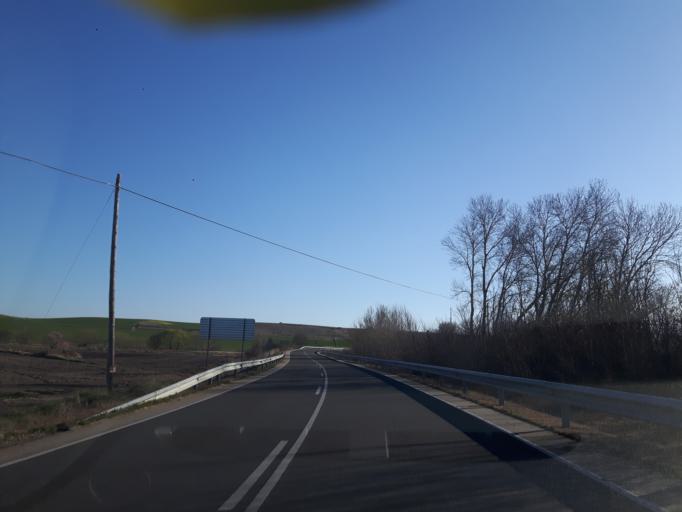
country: ES
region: Castille and Leon
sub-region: Provincia de Salamanca
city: Garcihernandez
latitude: 40.8609
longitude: -5.4218
